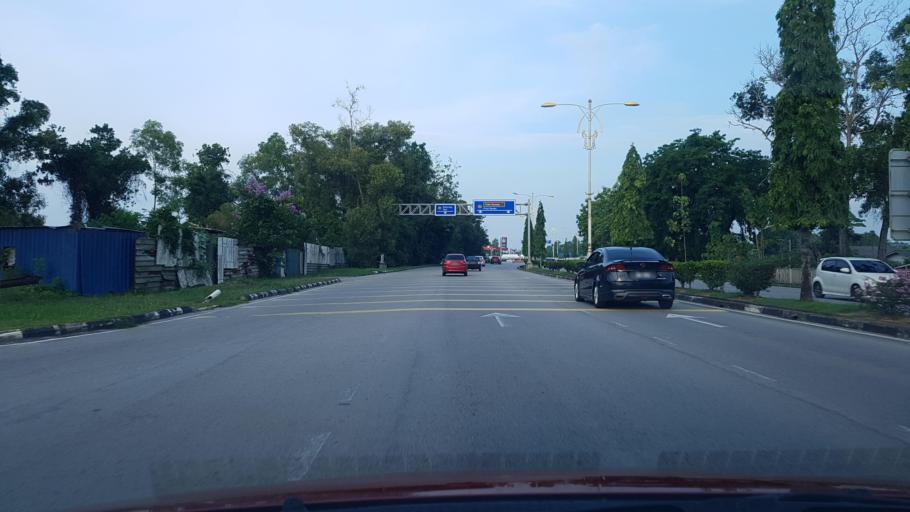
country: MY
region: Terengganu
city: Kuala Terengganu
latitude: 5.3390
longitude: 103.1100
